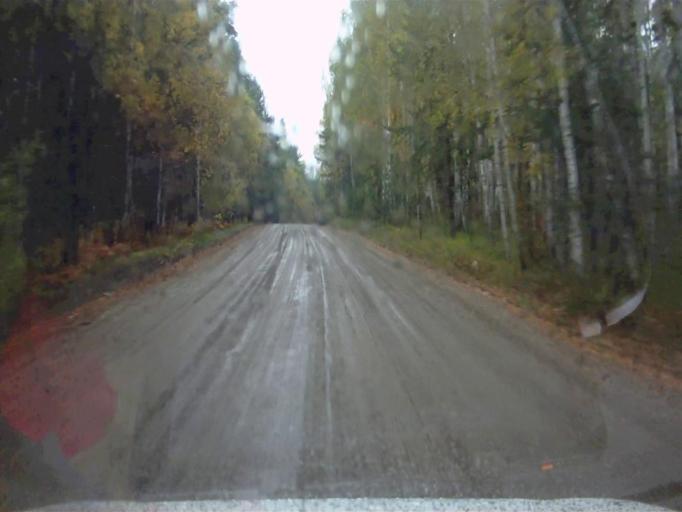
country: RU
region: Chelyabinsk
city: Kyshtym
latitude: 55.8862
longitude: 60.4654
